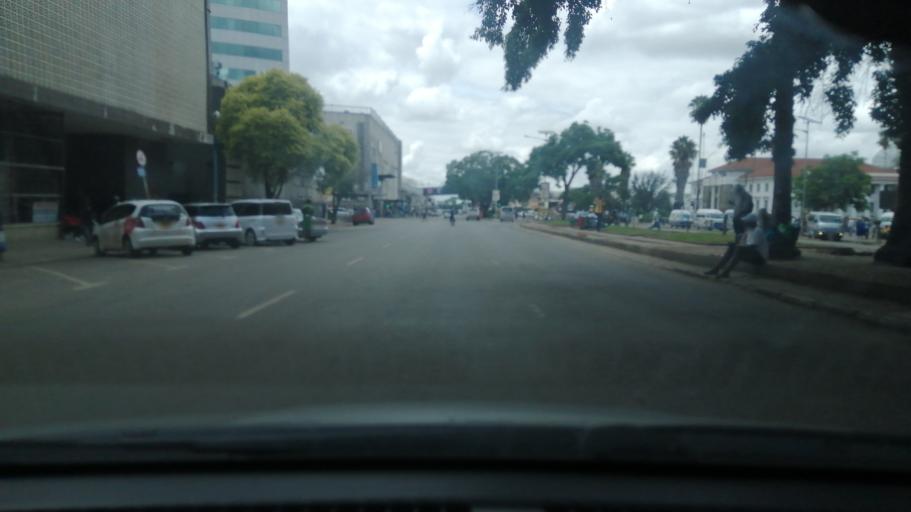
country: ZW
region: Harare
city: Harare
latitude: -17.8305
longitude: 31.0469
